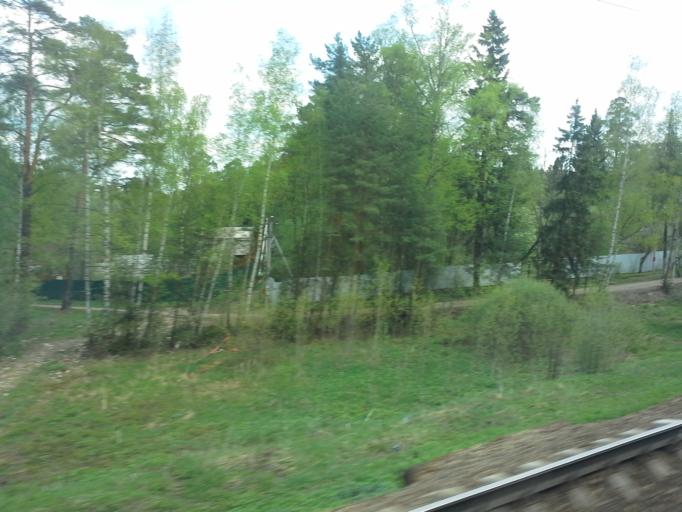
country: RU
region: Moskovskaya
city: Zelenogradskiy
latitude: 56.1004
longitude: 37.9072
